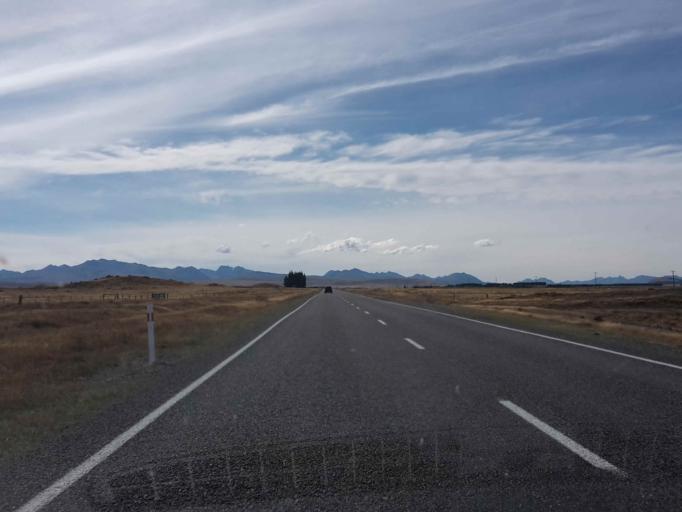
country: NZ
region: Canterbury
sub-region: Timaru District
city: Pleasant Point
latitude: -44.1321
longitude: 170.3496
